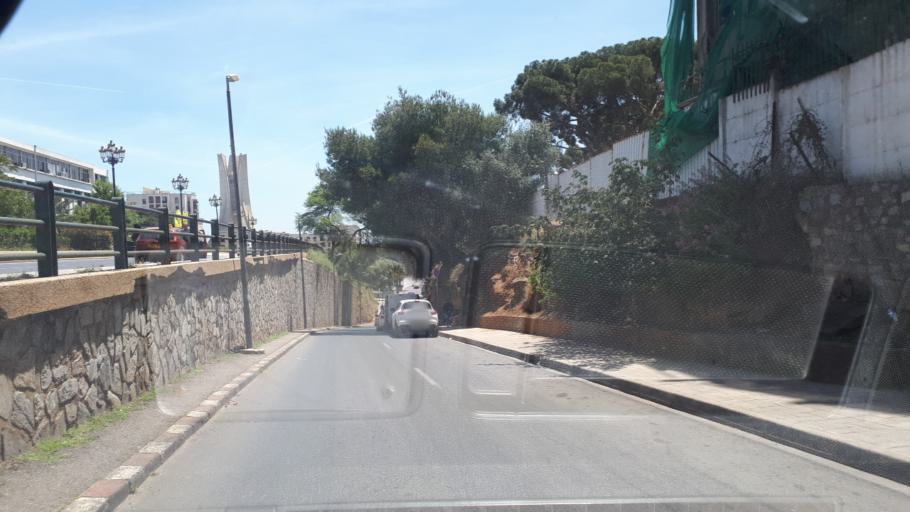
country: DZ
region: Alger
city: Algiers
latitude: 36.7471
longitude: 3.0627
